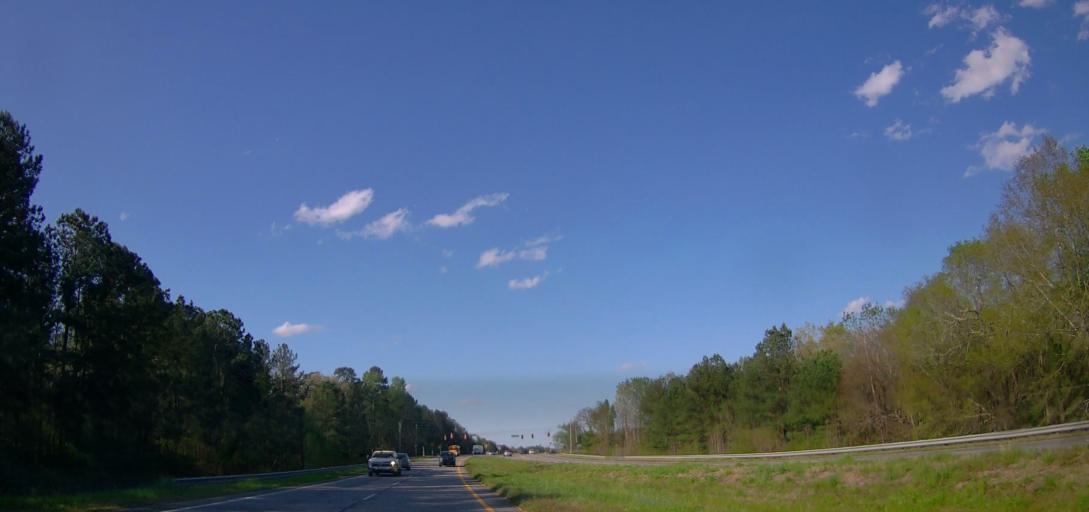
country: US
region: Georgia
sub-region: Baldwin County
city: Hardwick
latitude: 33.0497
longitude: -83.2553
